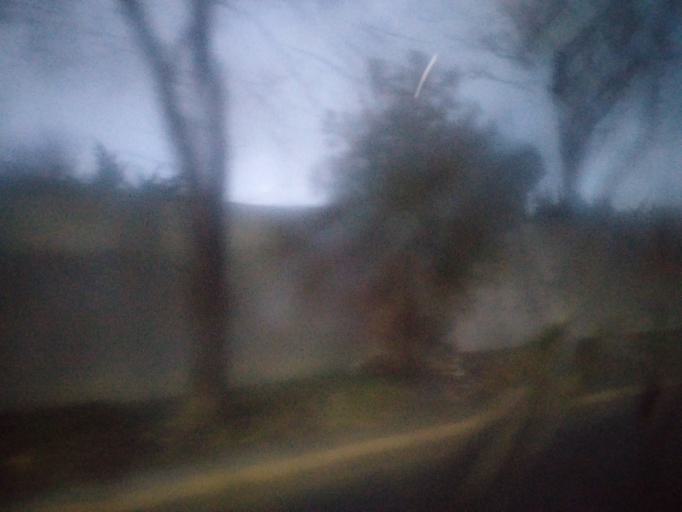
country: TR
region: Ankara
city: Ankara
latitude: 39.9574
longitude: 32.8223
